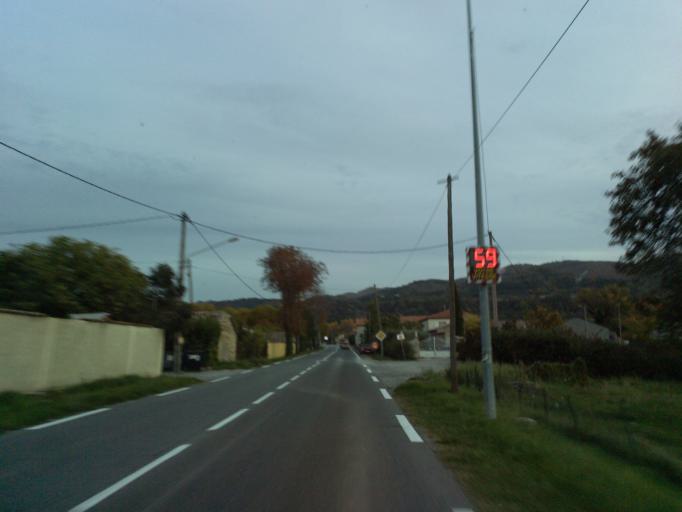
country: FR
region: Provence-Alpes-Cote d'Azur
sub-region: Departement des Alpes-de-Haute-Provence
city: Malijai
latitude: 44.0499
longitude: 6.0251
